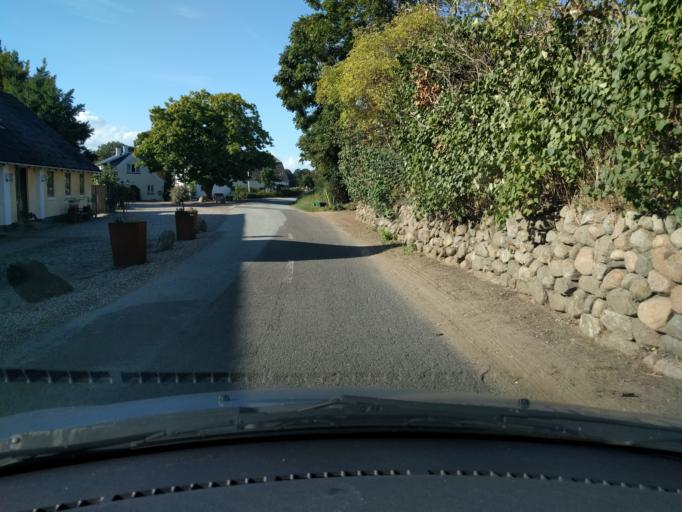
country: DK
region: South Denmark
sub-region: Assens Kommune
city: Harby
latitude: 55.1349
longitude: 10.0270
